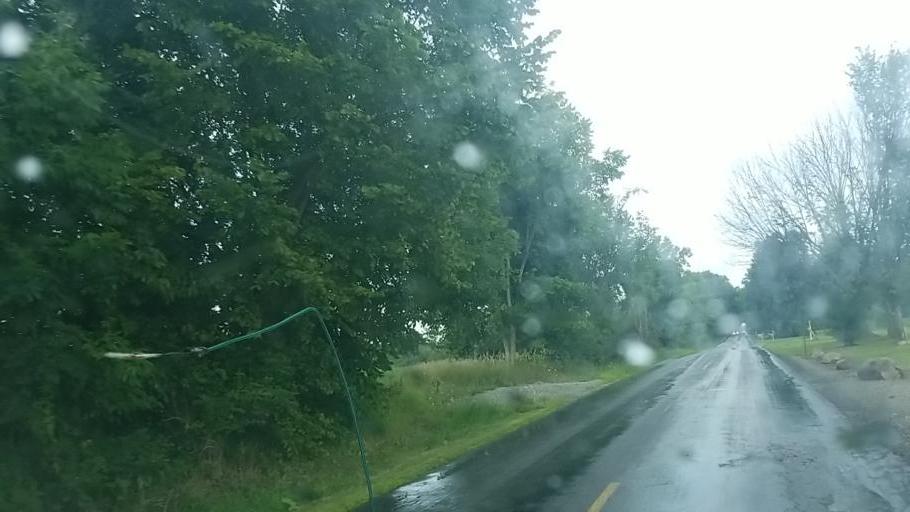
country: US
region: Ohio
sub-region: Lorain County
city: Lagrange
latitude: 41.1792
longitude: -82.0534
